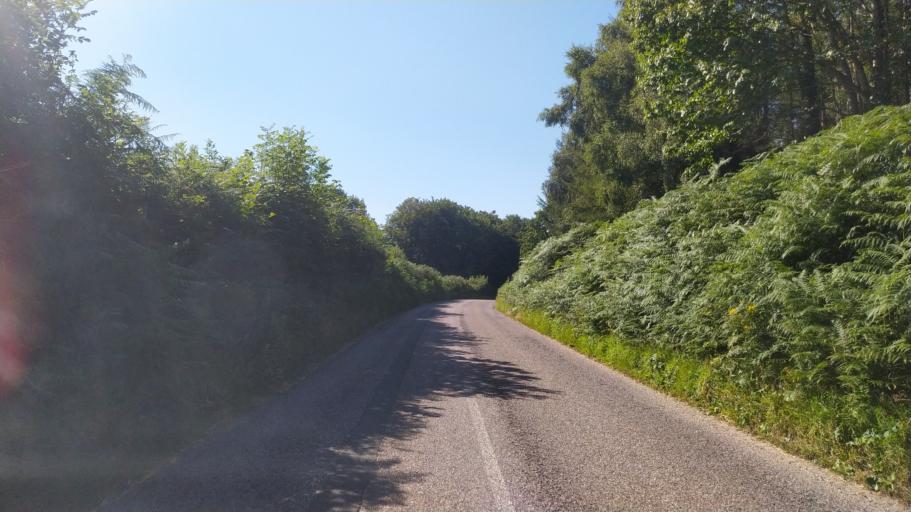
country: GB
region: England
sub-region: Dorset
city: Lytchett Matravers
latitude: 50.7568
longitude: -2.1269
